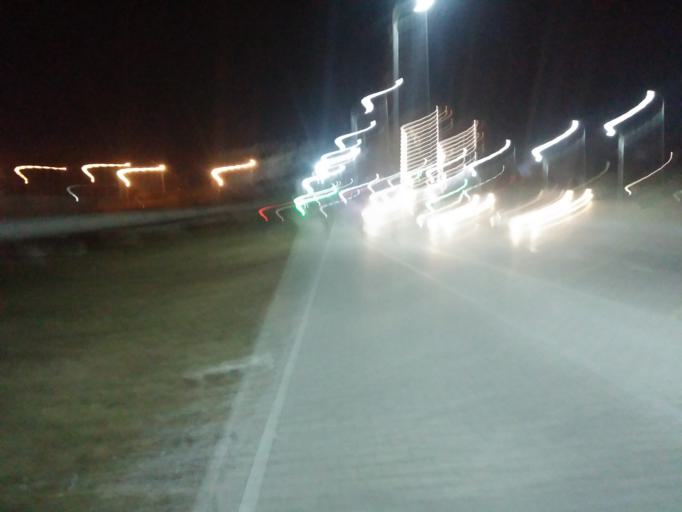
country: RU
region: Khabarovsk Krai
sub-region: Khabarovskiy Rayon
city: Khabarovsk
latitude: 48.4528
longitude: 135.0963
